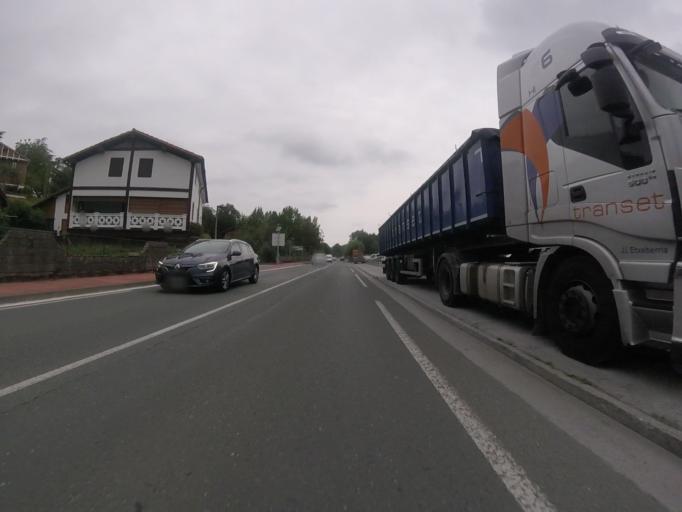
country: ES
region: Basque Country
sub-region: Provincia de Guipuzcoa
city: Errenteria
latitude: 43.2995
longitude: -1.8777
